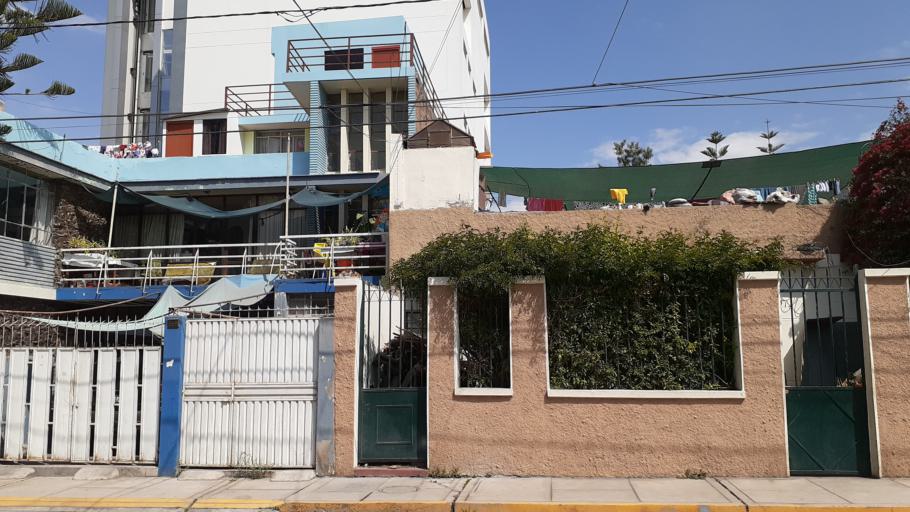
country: PE
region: Arequipa
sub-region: Provincia de Arequipa
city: Arequipa
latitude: -16.4077
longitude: -71.5371
